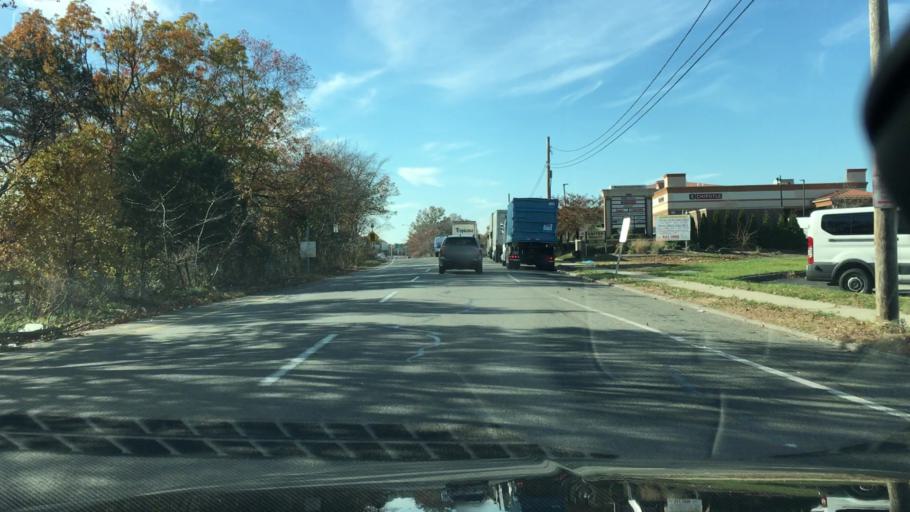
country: US
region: New York
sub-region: Suffolk County
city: Brentwood
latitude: 40.8070
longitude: -73.2362
